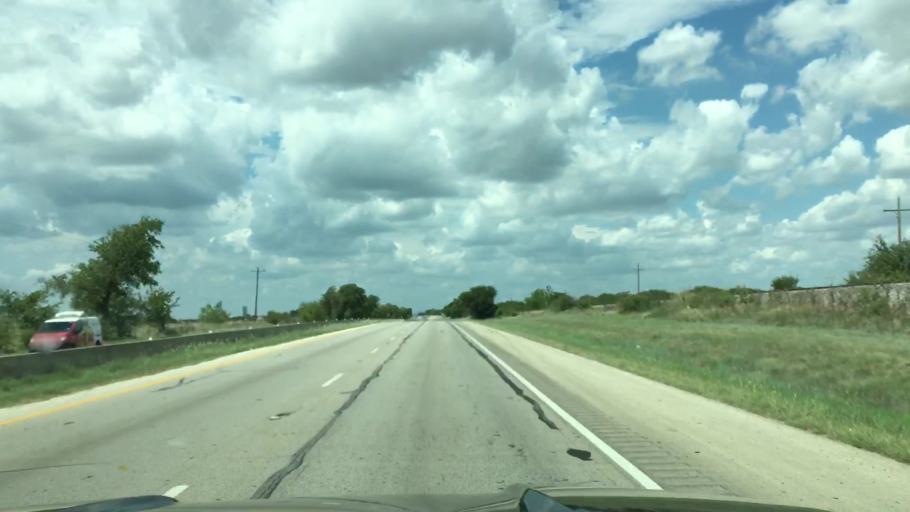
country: US
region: Texas
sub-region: Tarrant County
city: Eagle Mountain
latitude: 32.9118
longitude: -97.4057
